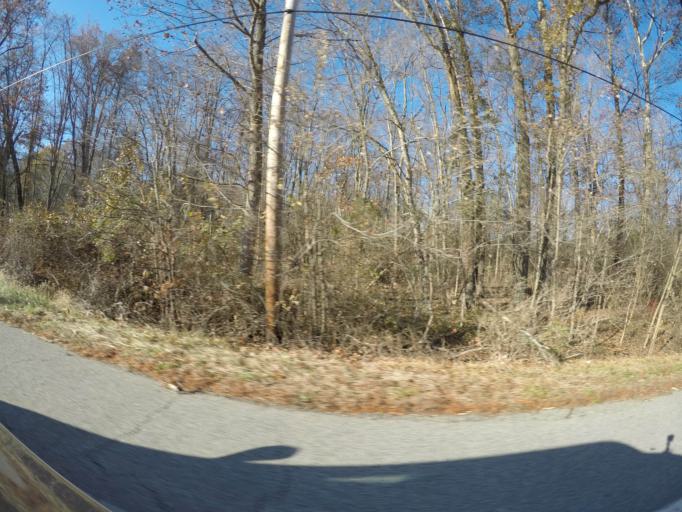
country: US
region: Maryland
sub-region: Cecil County
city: Rising Sun
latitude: 39.6847
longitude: -76.1417
